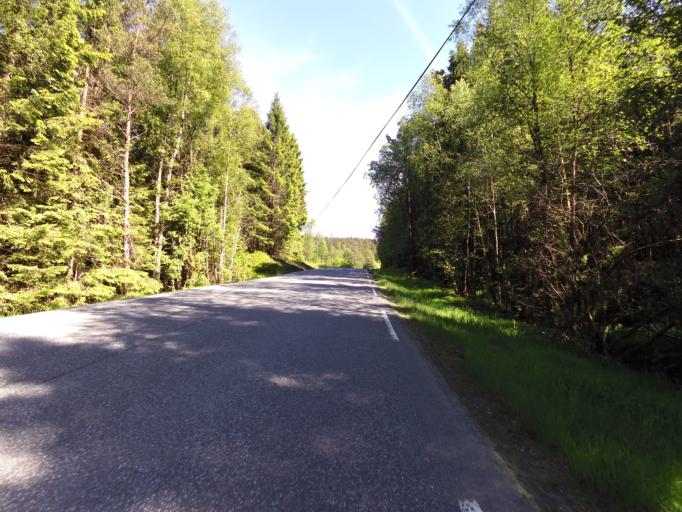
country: NO
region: Hordaland
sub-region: Stord
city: Leirvik
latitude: 59.7874
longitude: 5.4773
